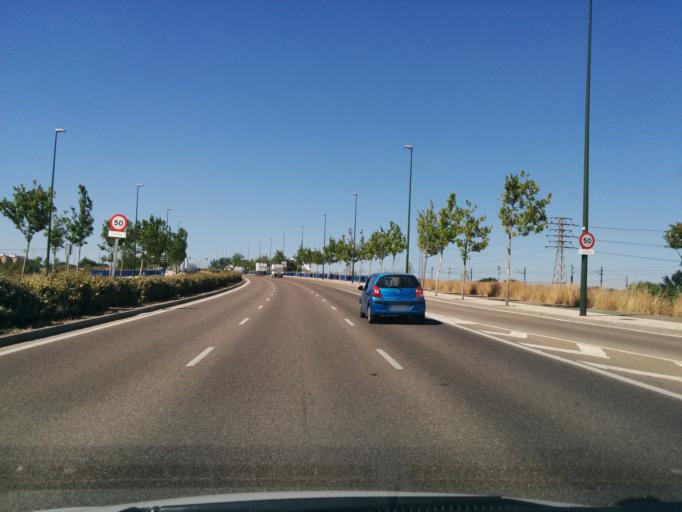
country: ES
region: Aragon
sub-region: Provincia de Zaragoza
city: Zaragoza
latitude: 41.6456
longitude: -0.8563
